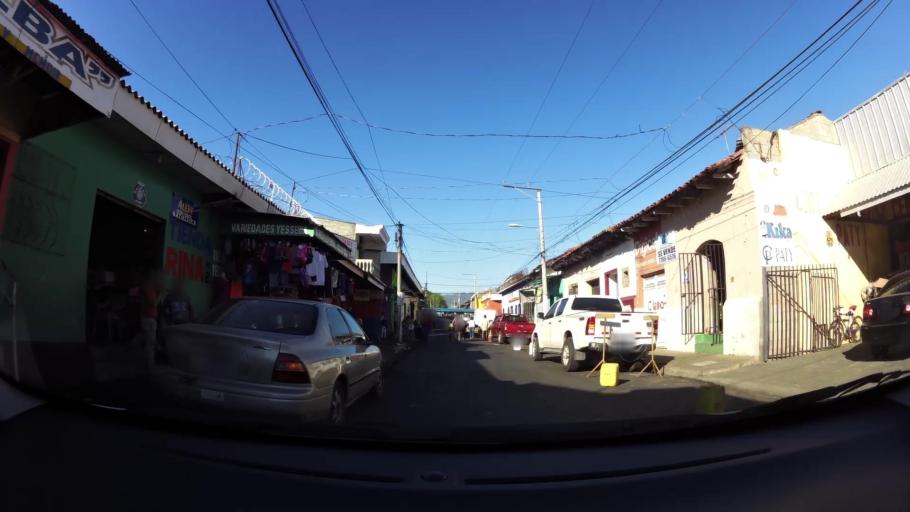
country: SV
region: San Miguel
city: San Miguel
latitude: 13.4794
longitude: -88.1779
